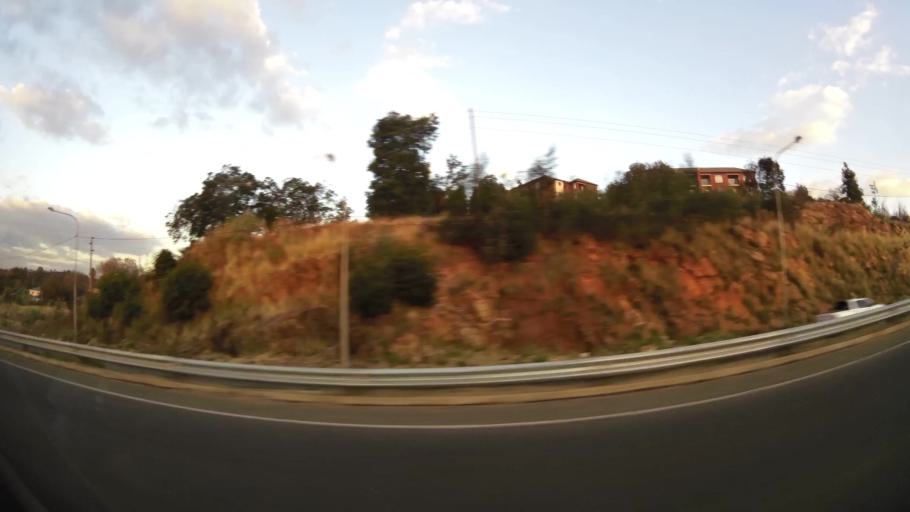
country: ZA
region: Gauteng
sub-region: West Rand District Municipality
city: Krugersdorp
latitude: -26.0745
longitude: 27.7986
